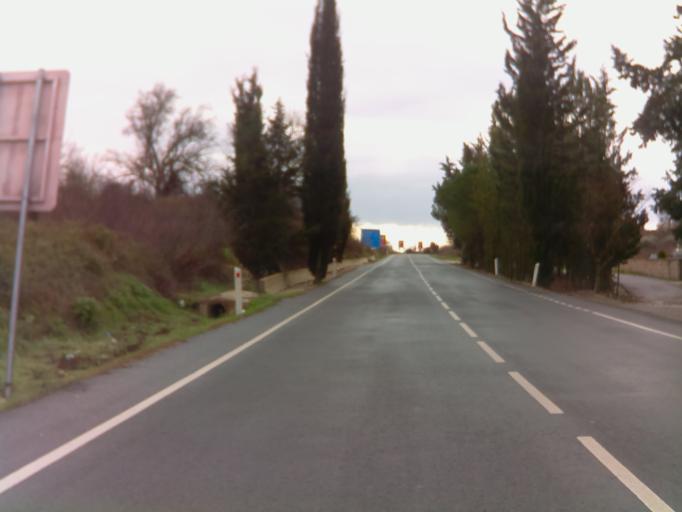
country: CY
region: Pafos
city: Pegeia
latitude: 34.9116
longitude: 32.4323
